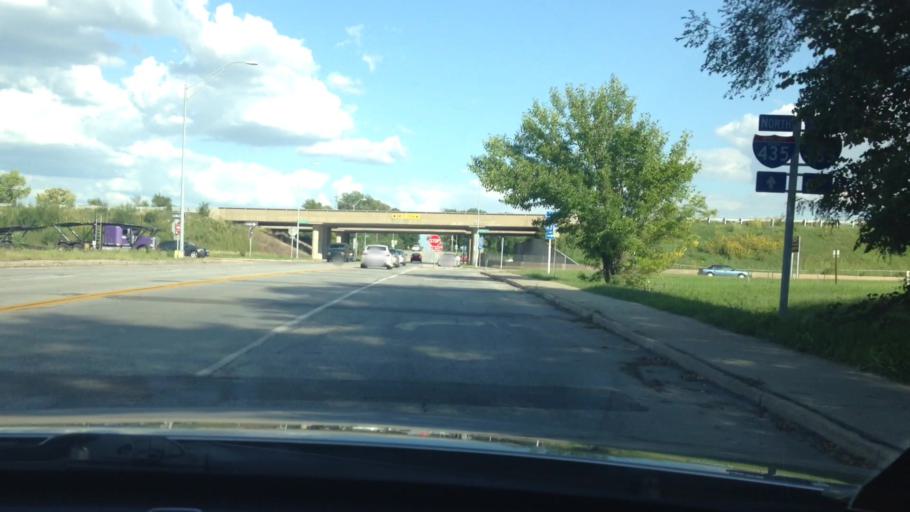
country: US
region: Missouri
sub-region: Clay County
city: Claycomo
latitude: 39.1805
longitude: -94.4946
